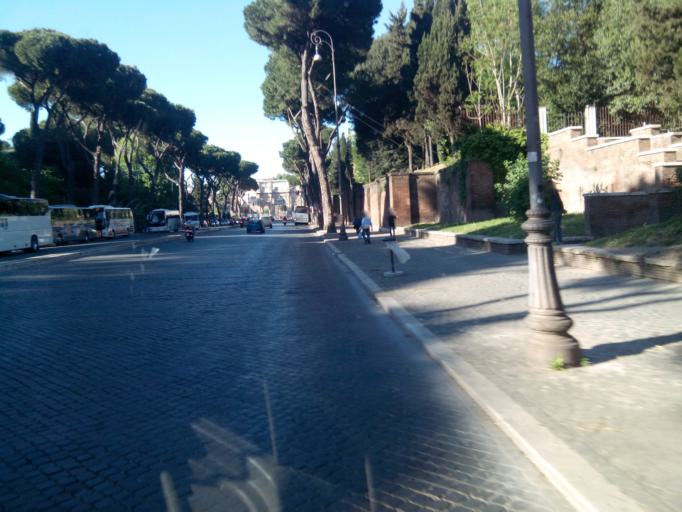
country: IT
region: Latium
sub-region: Citta metropolitana di Roma Capitale
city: Rome
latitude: 41.8865
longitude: 12.4900
